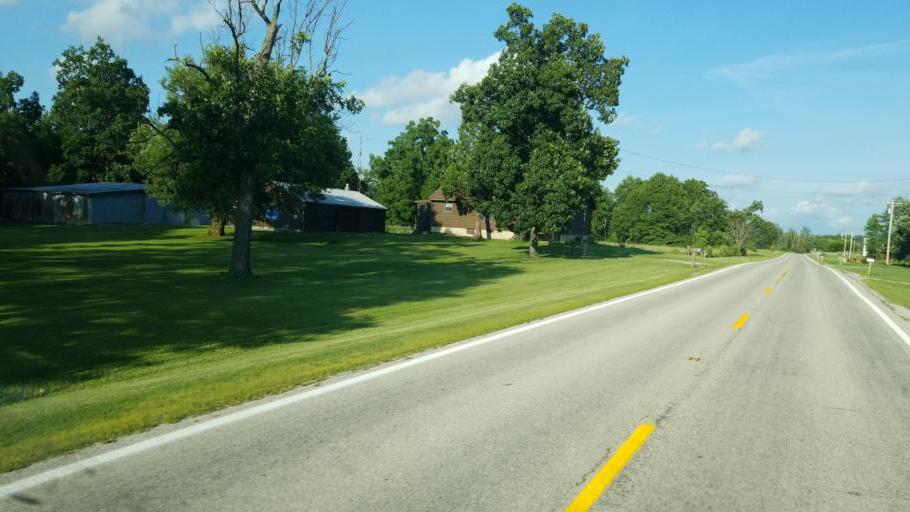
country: US
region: Ohio
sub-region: Union County
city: Richwood
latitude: 40.5783
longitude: -83.3503
